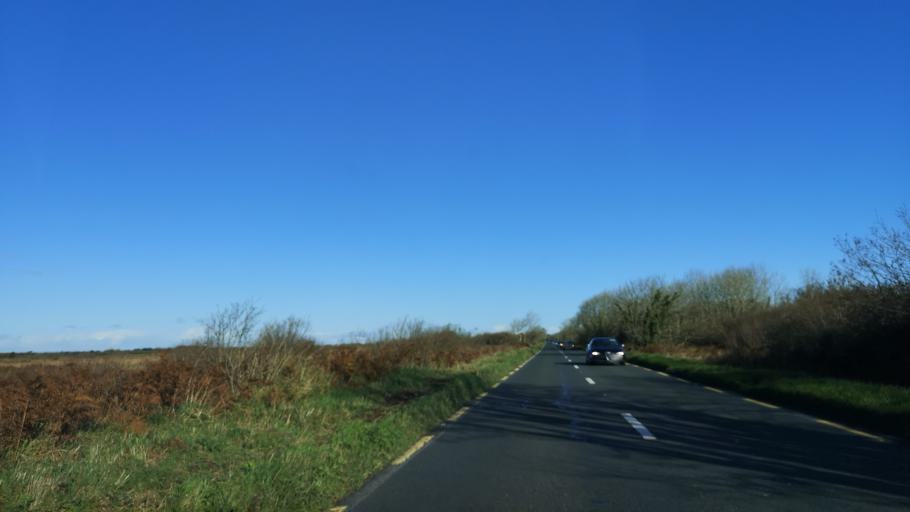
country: IE
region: Connaught
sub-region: County Galway
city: Claregalway
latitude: 53.3509
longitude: -9.0184
